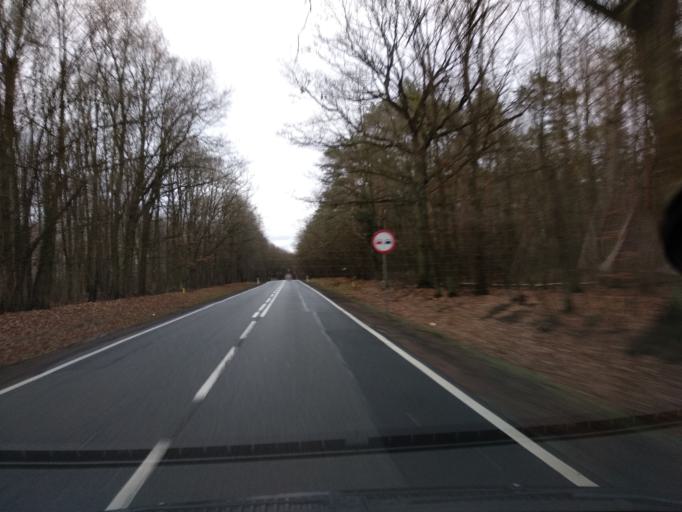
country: PL
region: Lower Silesian Voivodeship
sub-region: Powiat olesnicki
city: Olesnica
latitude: 51.2375
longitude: 17.4566
